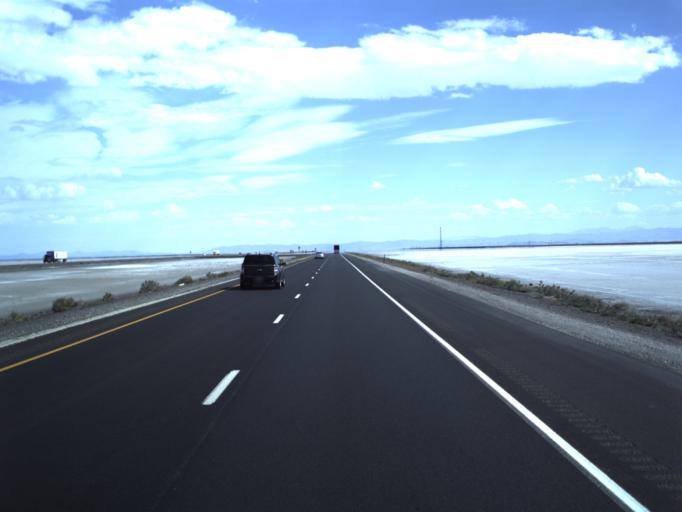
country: US
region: Utah
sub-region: Tooele County
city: Wendover
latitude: 40.7332
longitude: -113.6011
